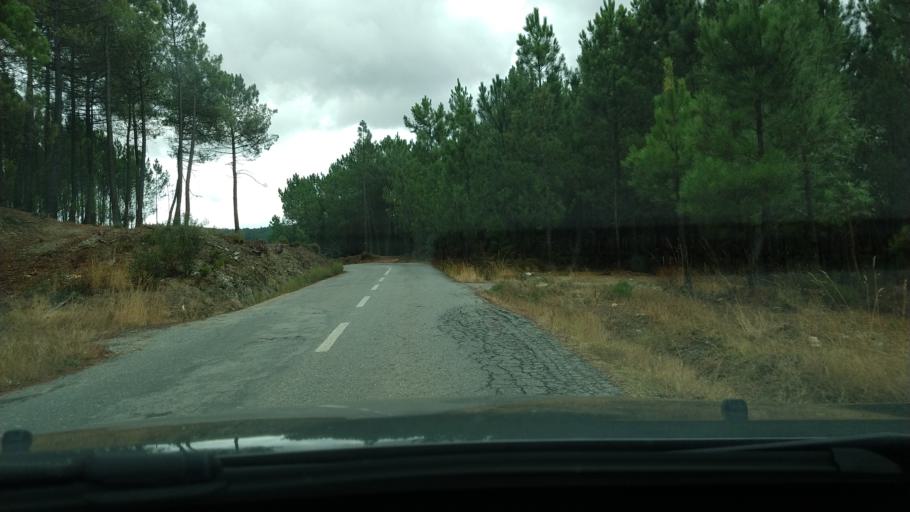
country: PT
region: Castelo Branco
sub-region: Concelho do Fundao
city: Aldeia de Joanes
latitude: 40.2208
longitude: -7.6330
